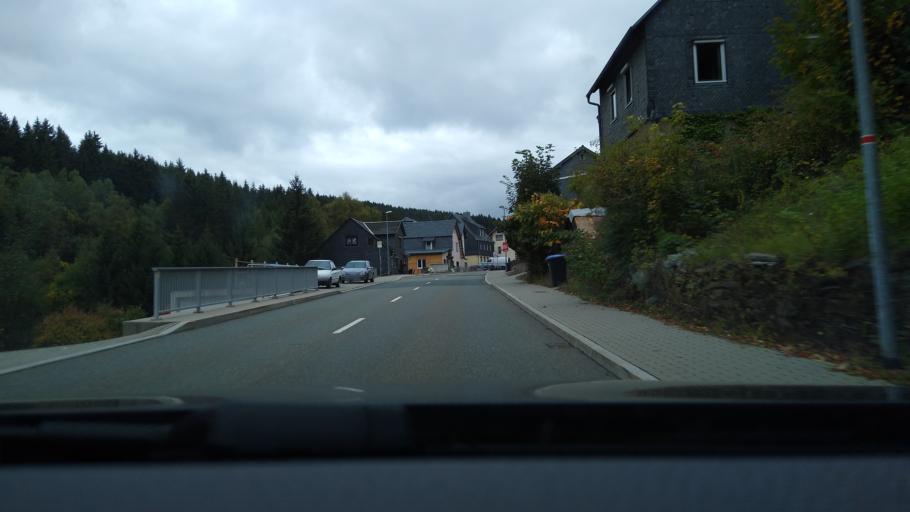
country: DE
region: Thuringia
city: Lichte
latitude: 50.5220
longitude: 11.1872
